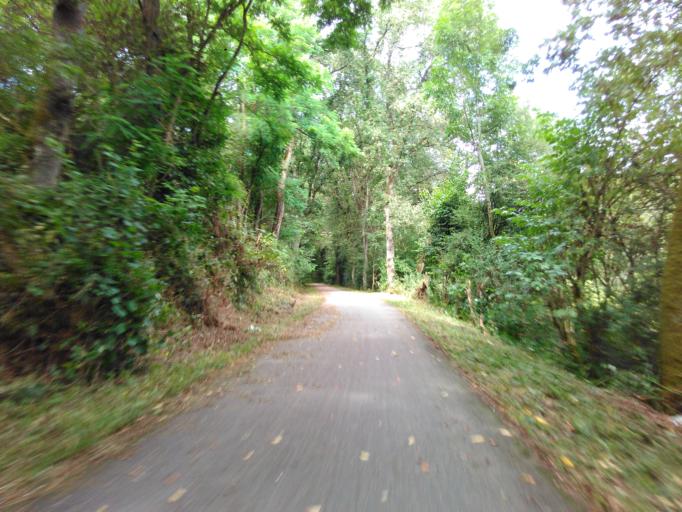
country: LU
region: Grevenmacher
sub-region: Canton d'Echternach
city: Consdorf
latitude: 49.7837
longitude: 6.3618
